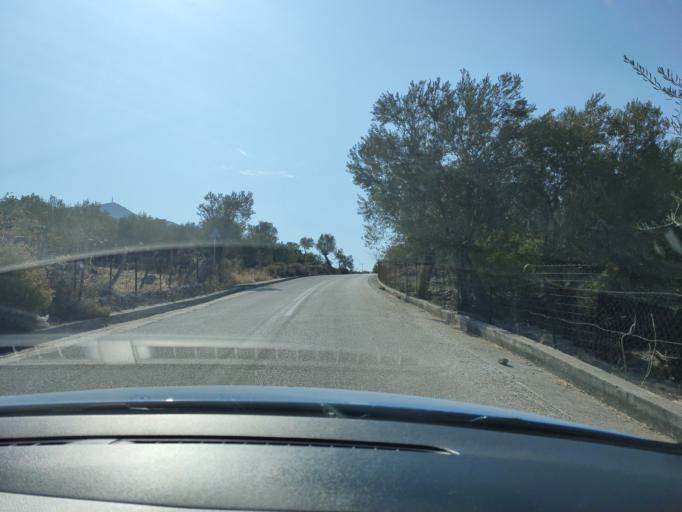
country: GR
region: North Aegean
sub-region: Nomos Lesvou
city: Mantamados
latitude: 39.3724
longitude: 26.3073
